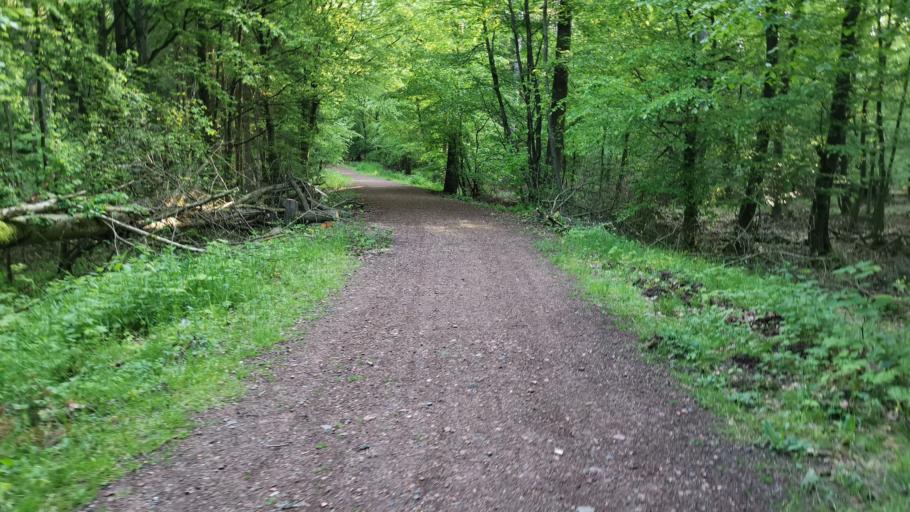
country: DE
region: Saarland
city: Sankt Ingbert
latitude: 49.2703
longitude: 7.1741
